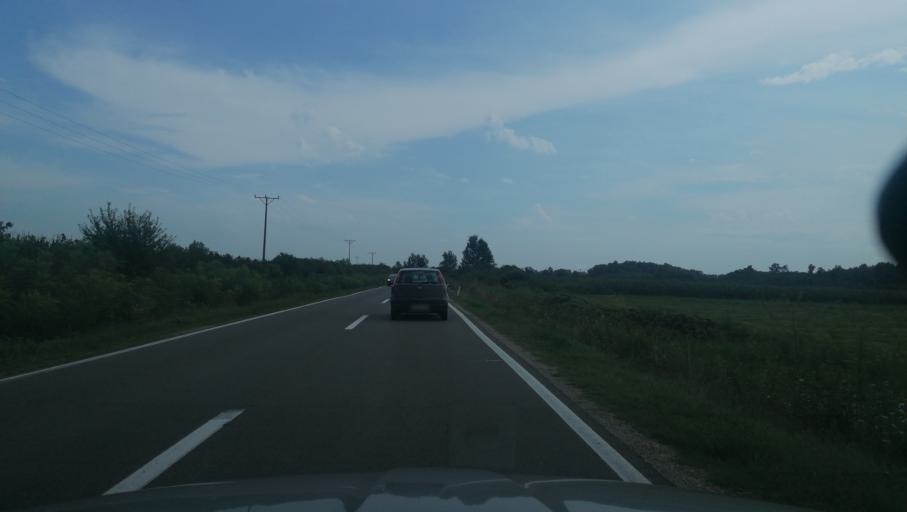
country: HR
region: Vukovarsko-Srijemska
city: Soljani
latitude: 44.8386
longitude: 18.9734
